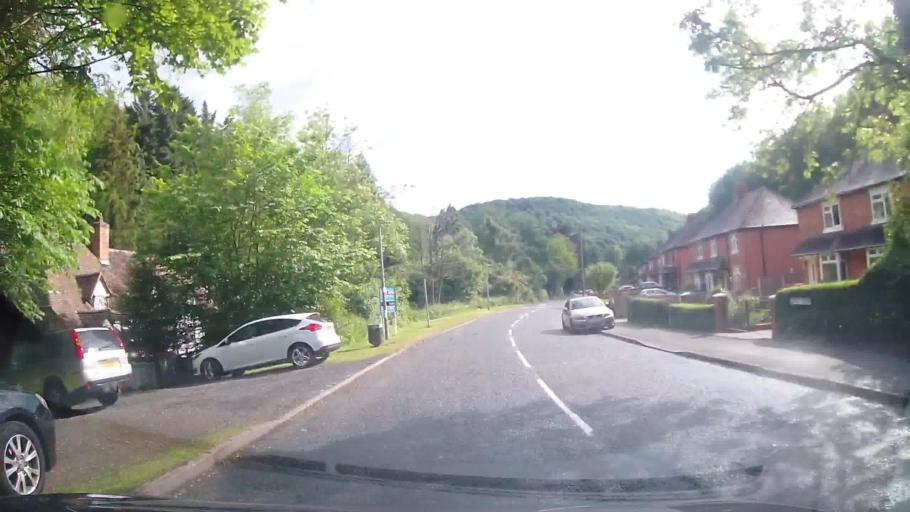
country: GB
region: England
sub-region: Telford and Wrekin
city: Ironbridge
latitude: 52.6338
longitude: -2.4912
